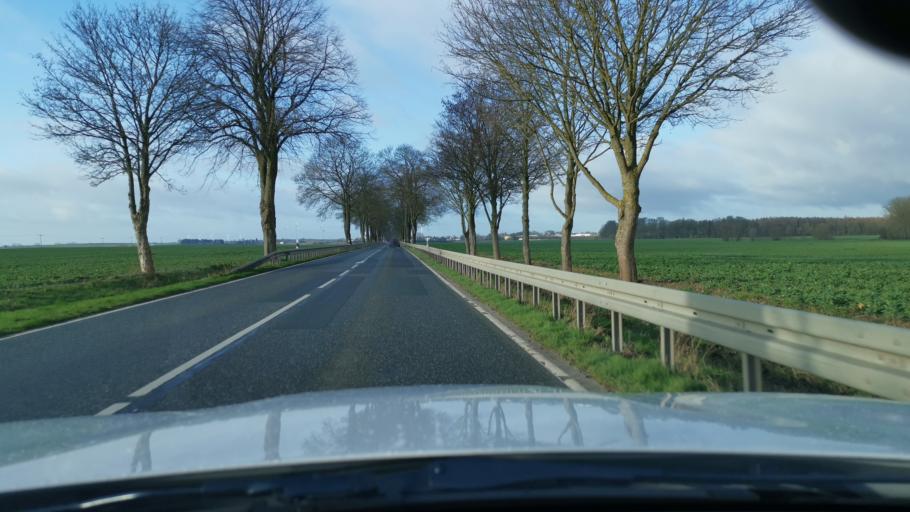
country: DE
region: Mecklenburg-Vorpommern
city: Laage
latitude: 53.8958
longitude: 12.2754
